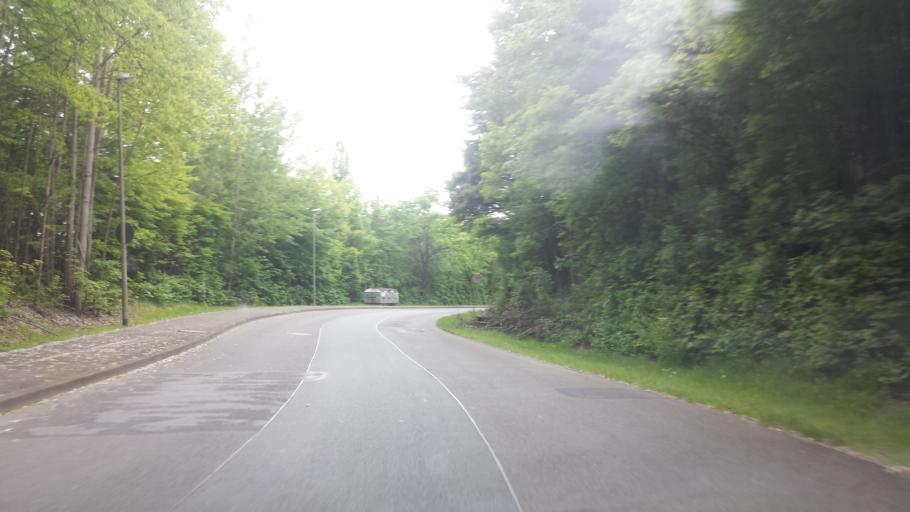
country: DE
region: Hesse
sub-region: Regierungsbezirk Darmstadt
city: Kronberg
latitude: 50.1932
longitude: 8.5129
